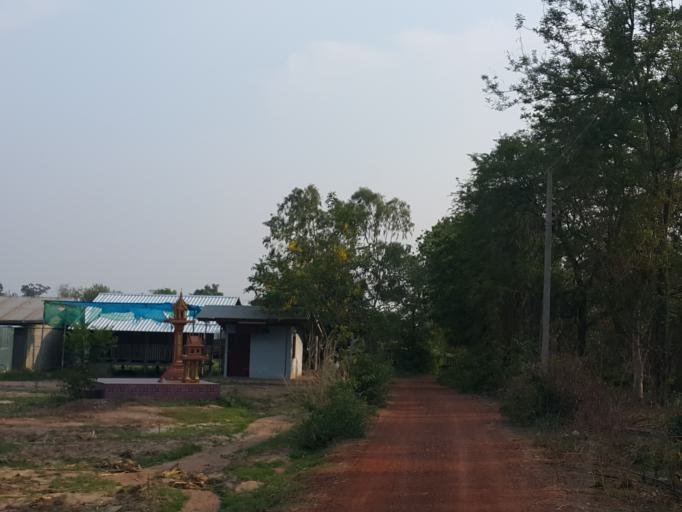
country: TH
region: Uthai Thani
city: Huai Khot
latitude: 15.3201
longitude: 99.6763
